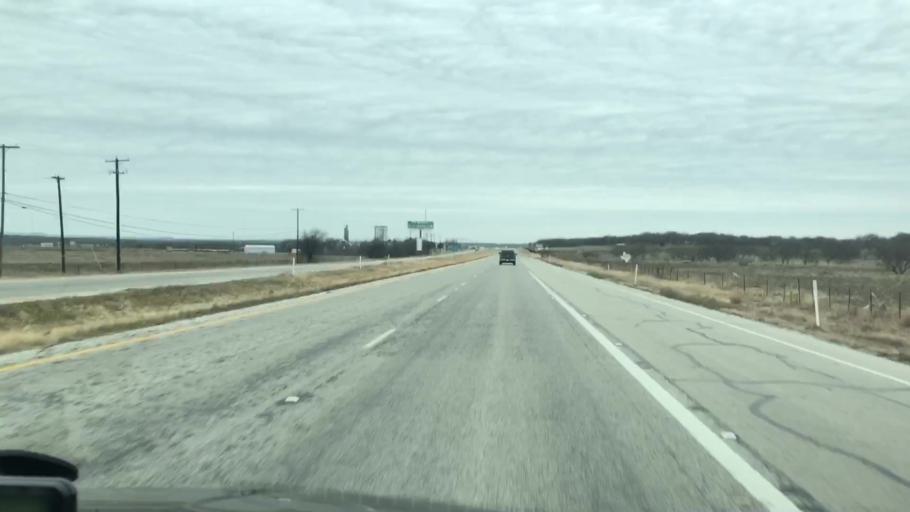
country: US
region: Texas
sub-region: Jack County
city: Jacksboro
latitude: 33.1909
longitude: -98.1365
